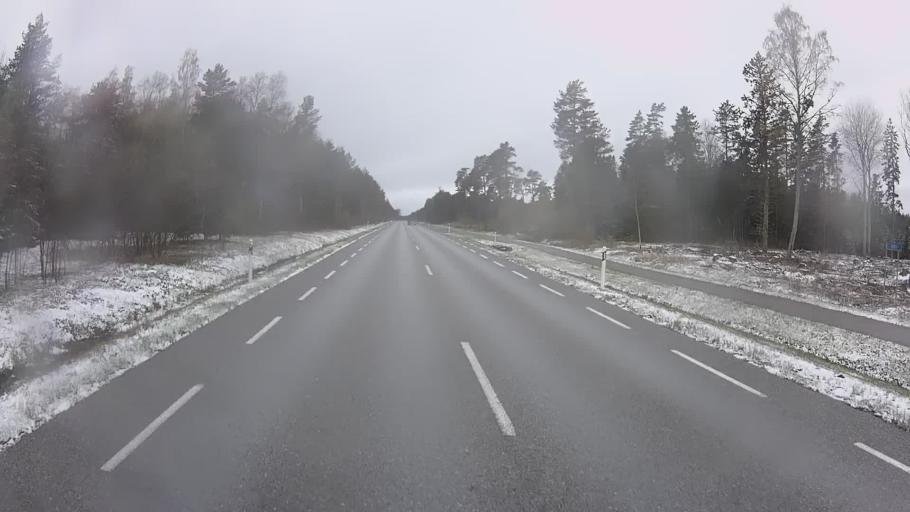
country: EE
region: Hiiumaa
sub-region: Kaerdla linn
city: Kardla
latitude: 59.0106
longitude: 22.6642
